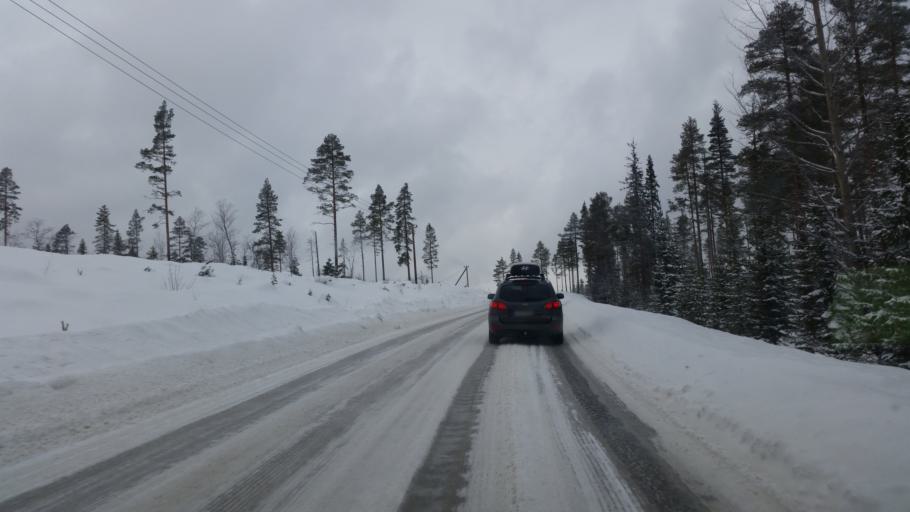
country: SE
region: Jaemtland
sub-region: Bergs Kommun
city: Hoverberg
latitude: 62.4734
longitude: 14.2613
